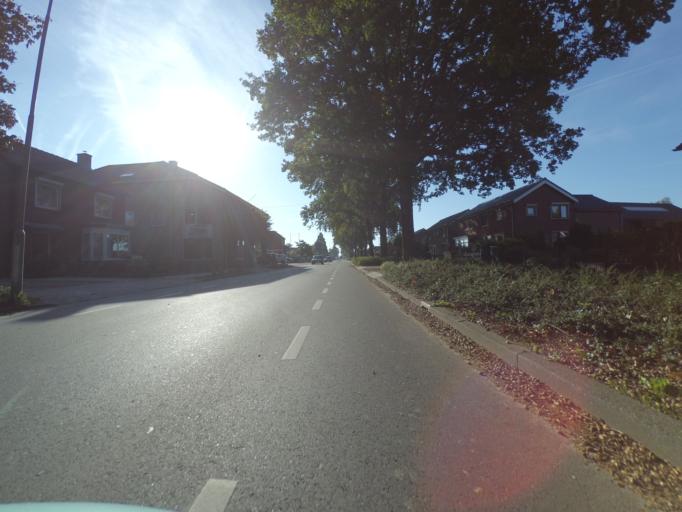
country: NL
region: Gelderland
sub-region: Gemeente Wageningen
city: Wageningen
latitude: 51.9310
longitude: 5.6350
